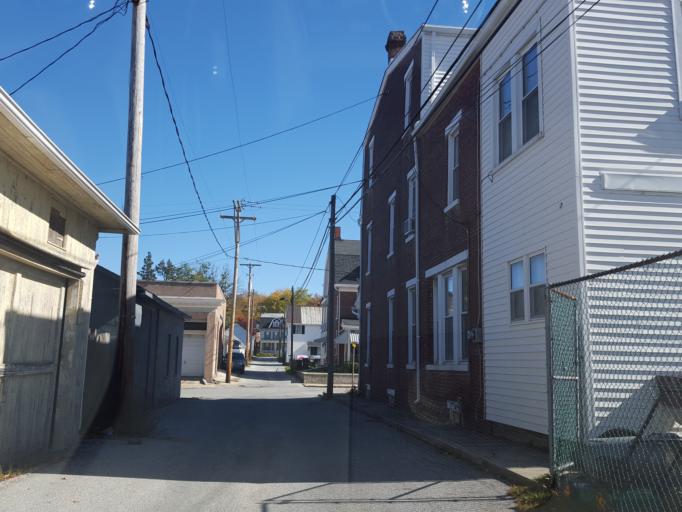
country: US
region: Pennsylvania
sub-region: York County
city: Red Lion
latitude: 39.8966
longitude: -76.6127
